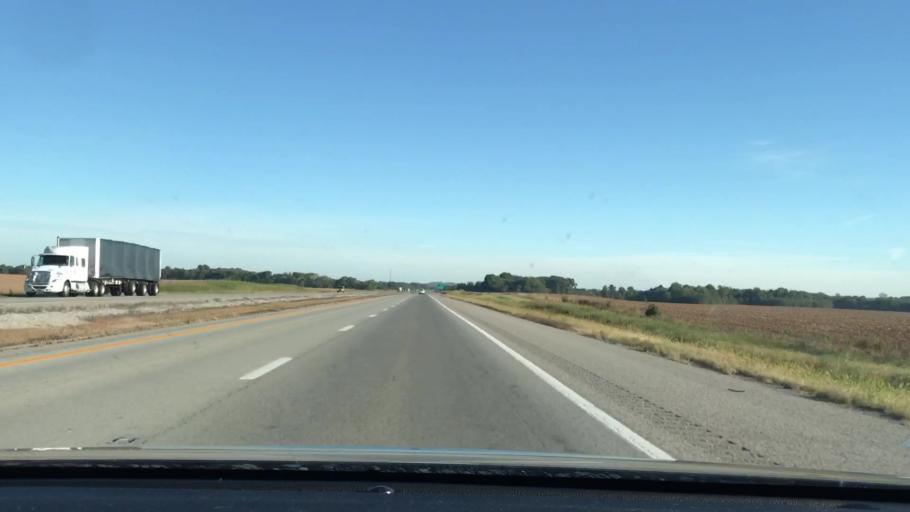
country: US
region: Kentucky
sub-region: Christian County
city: Hopkinsville
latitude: 36.7844
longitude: -87.4966
